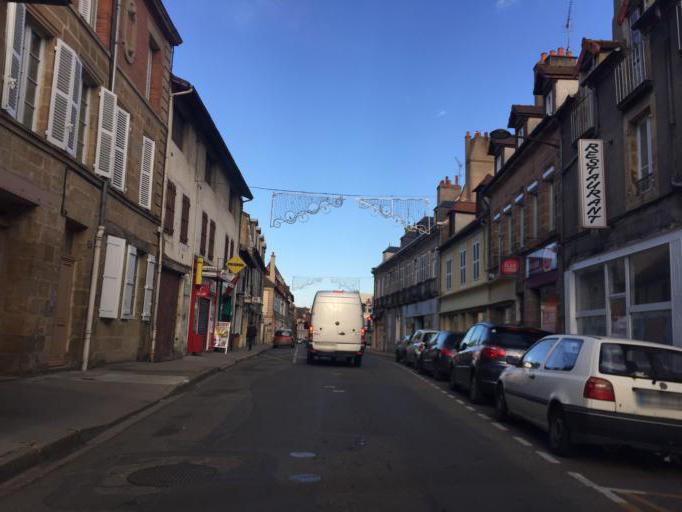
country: FR
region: Auvergne
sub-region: Departement de l'Allier
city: Moulins
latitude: 46.5606
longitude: 3.3335
